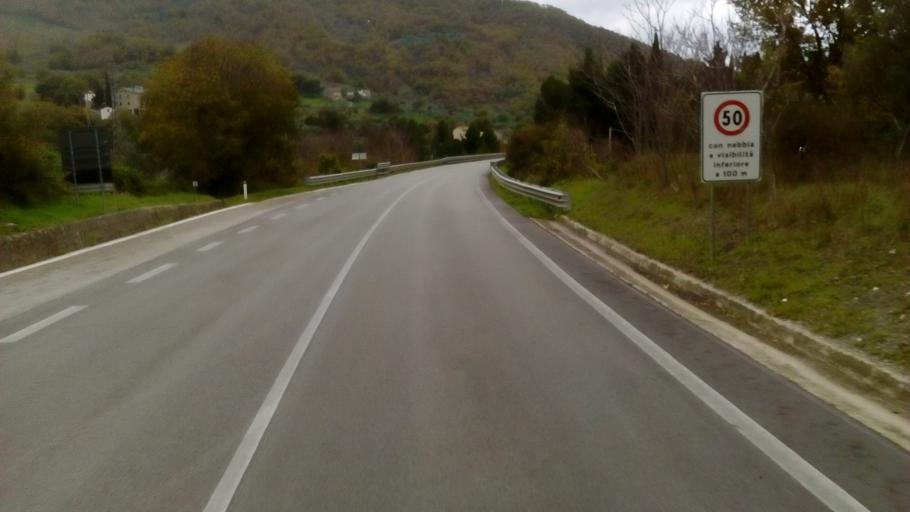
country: IT
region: Molise
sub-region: Provincia di Campobasso
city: Roccavivara
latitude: 41.8543
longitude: 14.6037
